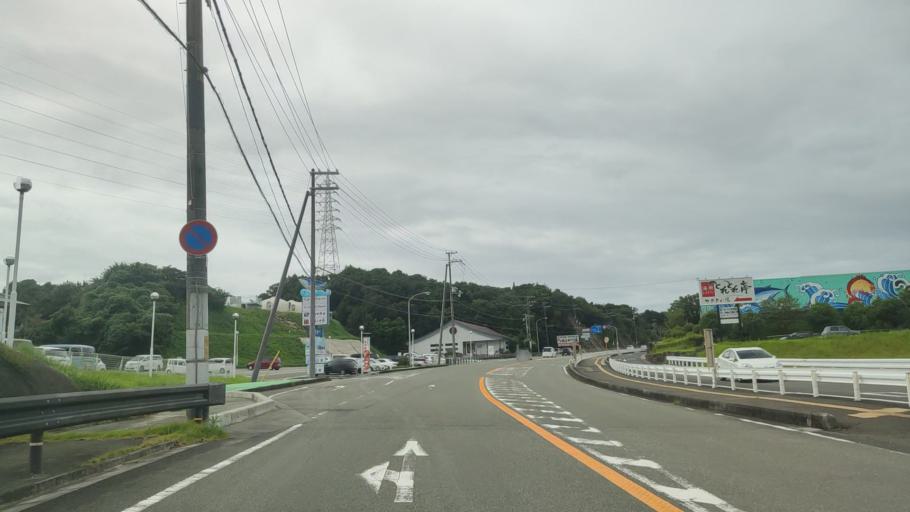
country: JP
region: Wakayama
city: Tanabe
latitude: 33.6815
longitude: 135.3772
